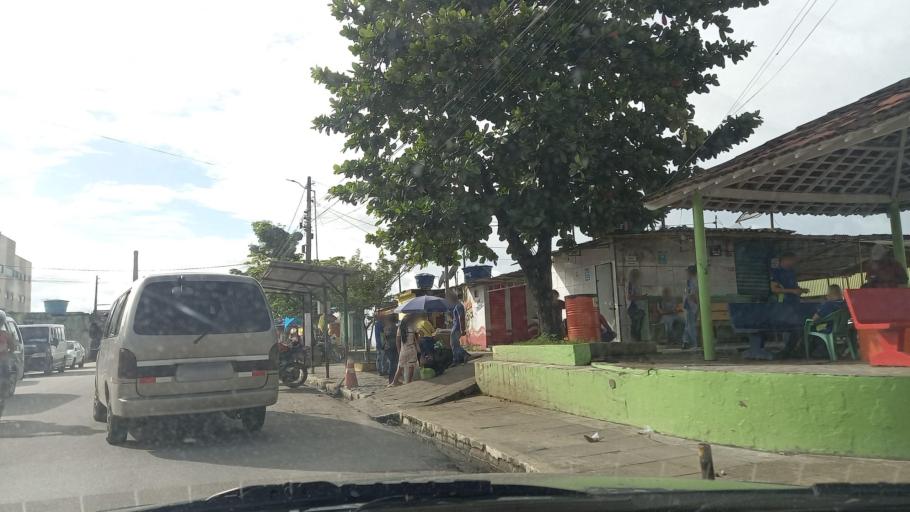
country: BR
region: Pernambuco
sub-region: Palmares
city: Palmares
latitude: -8.6867
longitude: -35.5958
